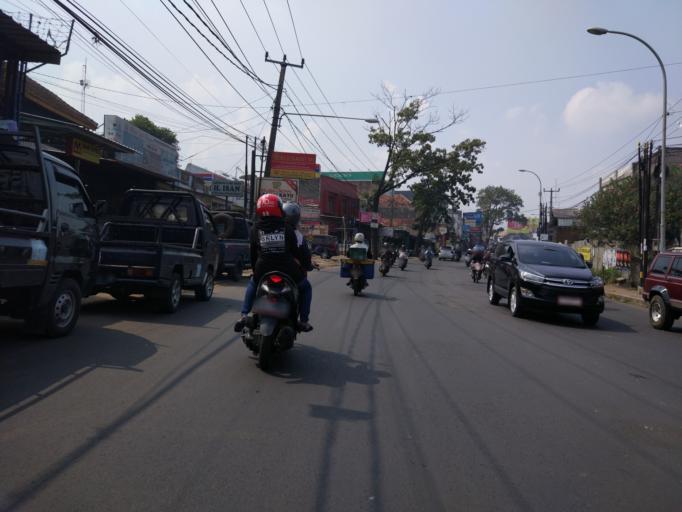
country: ID
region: West Java
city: Cileunyi
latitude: -6.9388
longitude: 107.7379
